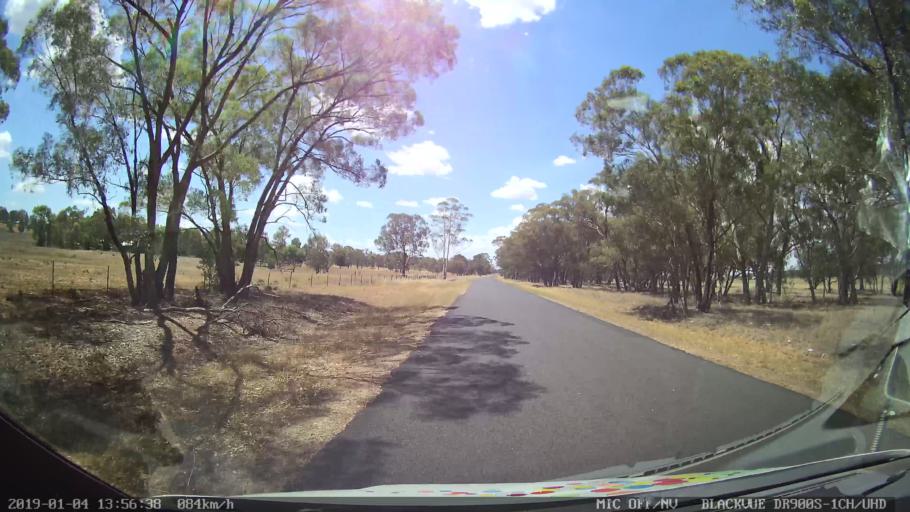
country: AU
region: New South Wales
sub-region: Dubbo Municipality
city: Dubbo
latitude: -32.3490
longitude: 148.5956
